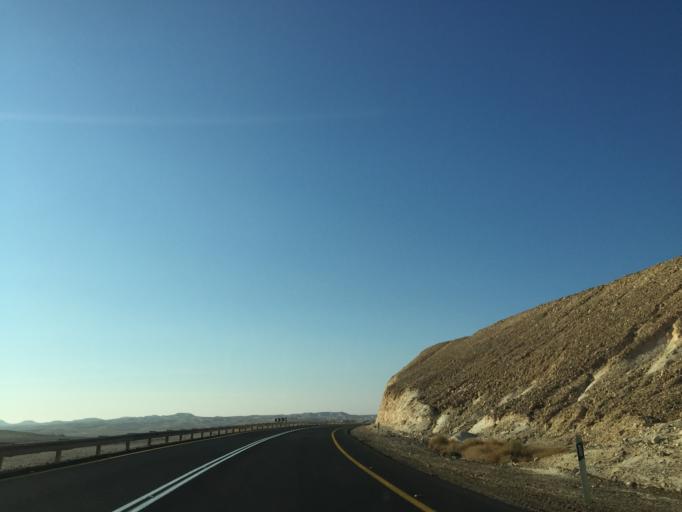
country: IL
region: Southern District
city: Mitzpe Ramon
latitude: 30.2386
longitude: 35.0225
